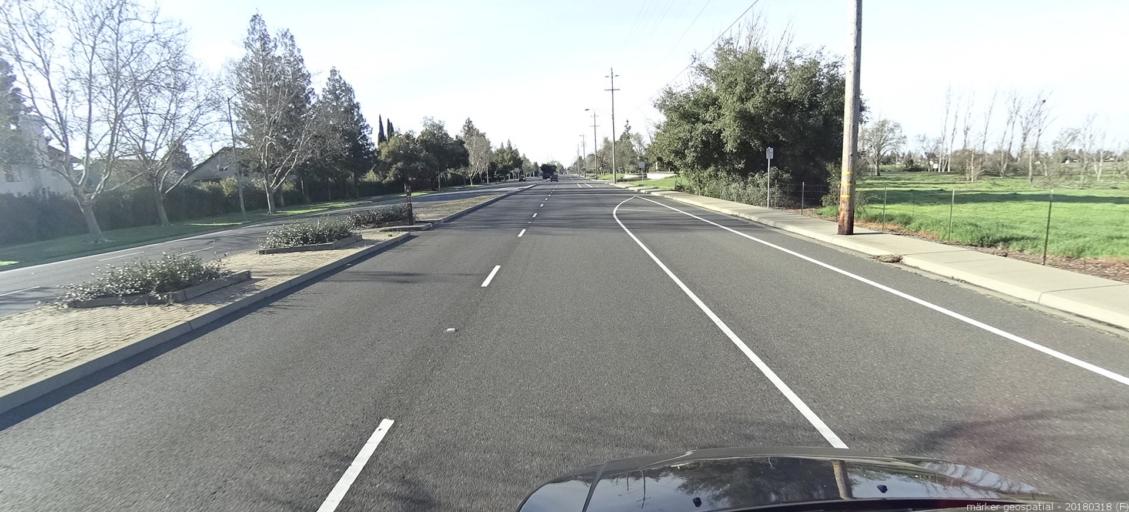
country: US
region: California
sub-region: Sacramento County
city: Laguna
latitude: 38.4389
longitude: -121.4456
